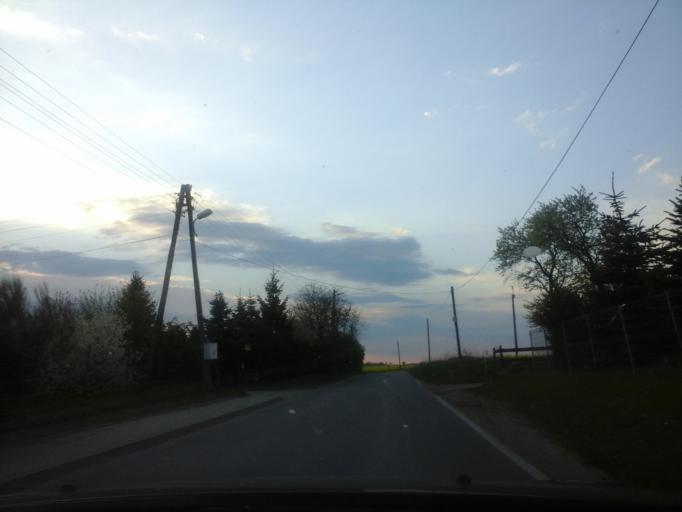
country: PL
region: West Pomeranian Voivodeship
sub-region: Powiat choszczenski
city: Pelczyce
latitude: 53.0251
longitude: 15.3656
